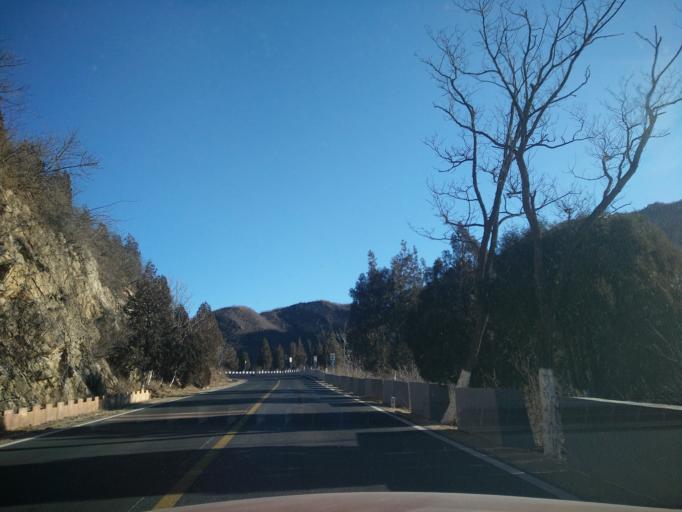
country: CN
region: Beijing
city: Wangping
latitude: 40.0084
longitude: 115.9792
